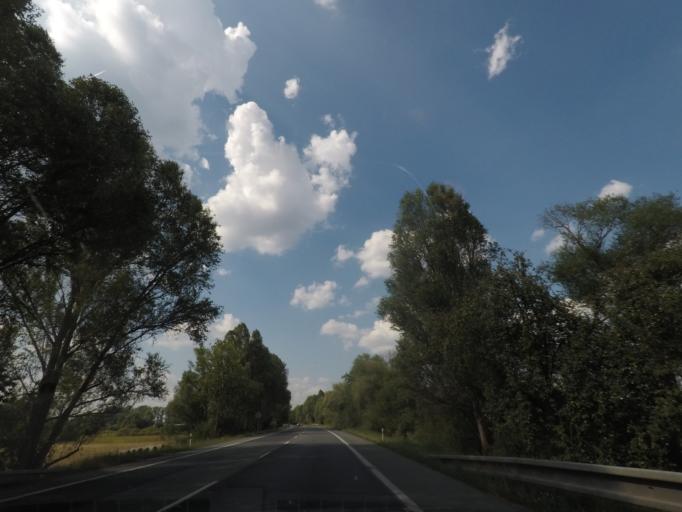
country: CZ
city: Tyniste nad Orlici
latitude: 50.1514
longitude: 16.0687
